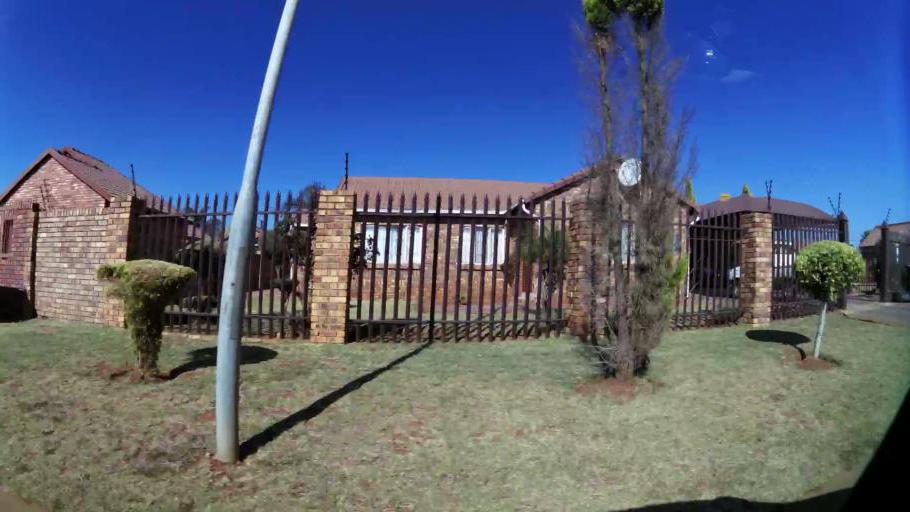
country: ZA
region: North-West
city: Ga-Rankuwa
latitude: -25.6645
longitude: 28.0863
